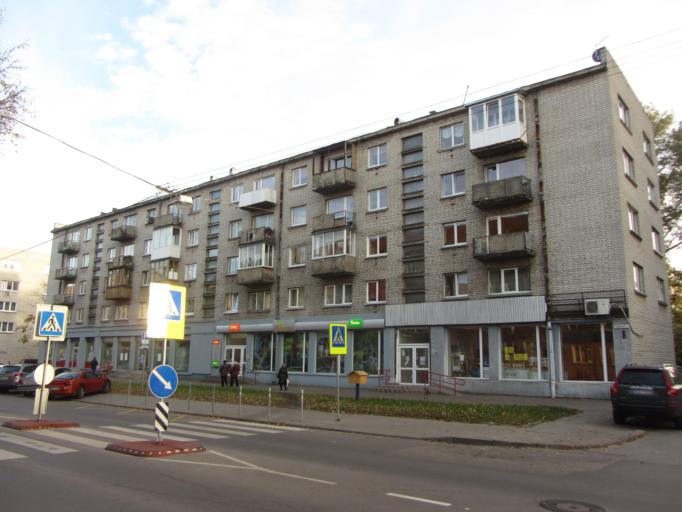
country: LT
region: Vilnius County
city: Naujamiestis
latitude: 54.6768
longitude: 25.2617
